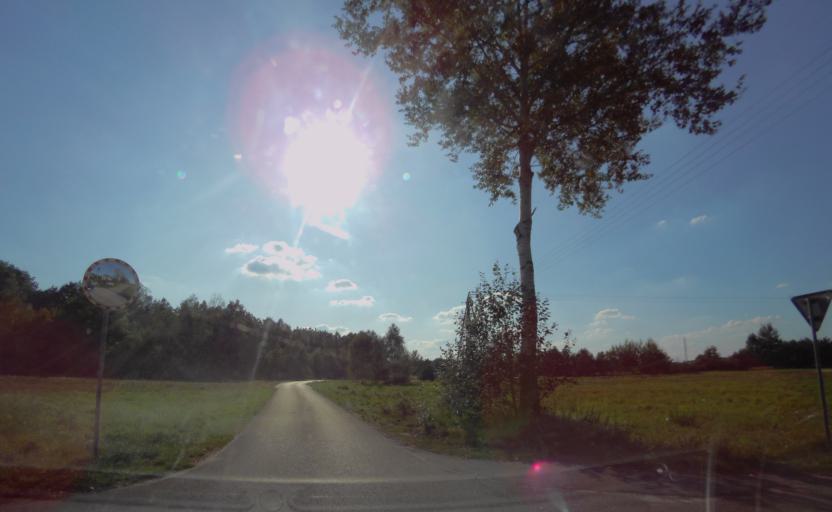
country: PL
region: Subcarpathian Voivodeship
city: Nowa Sarzyna
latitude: 50.2987
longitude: 22.3827
